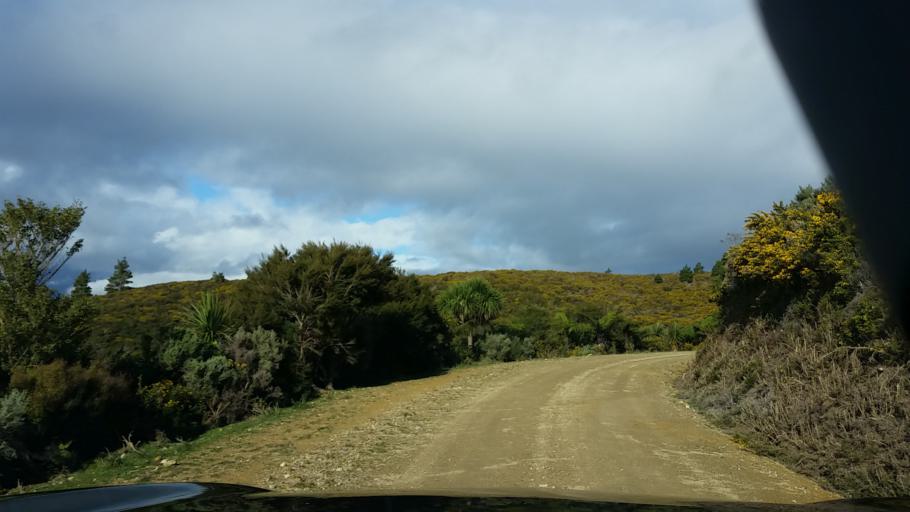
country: NZ
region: Marlborough
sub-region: Marlborough District
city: Picton
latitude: -40.9704
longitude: 173.8928
